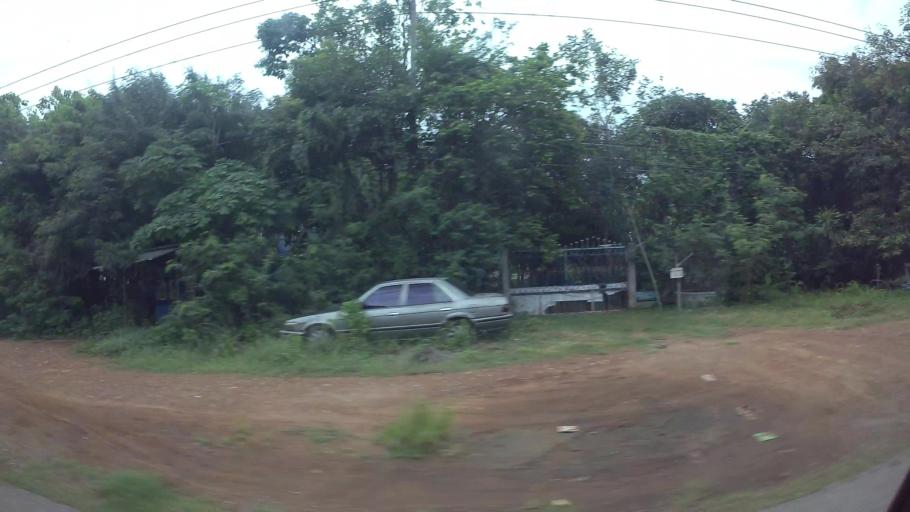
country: TH
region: Chon Buri
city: Si Racha
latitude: 13.2032
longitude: 100.9473
